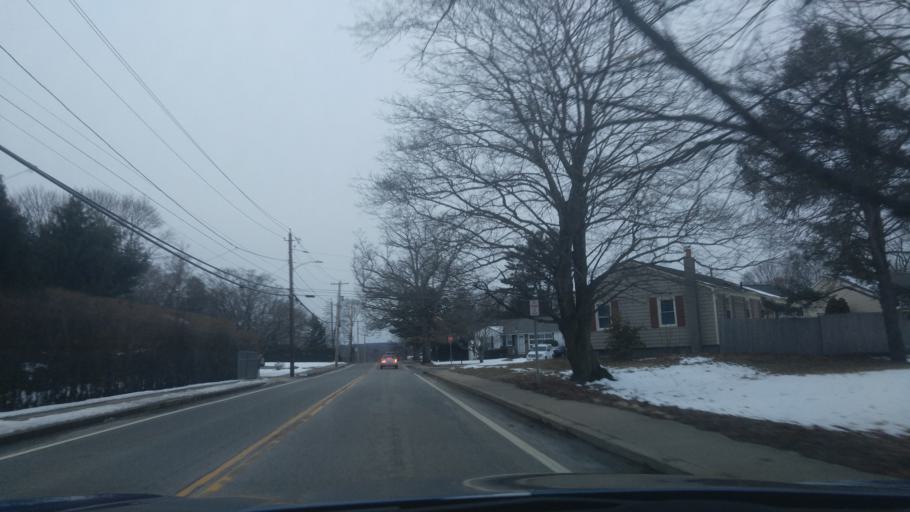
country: US
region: Rhode Island
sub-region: Providence County
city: Cranston
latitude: 41.7343
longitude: -71.4732
